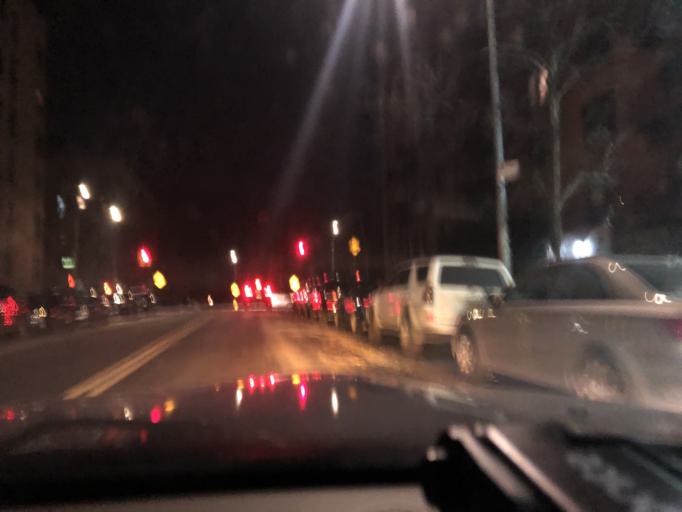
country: US
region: New York
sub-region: New York County
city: Inwood
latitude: 40.8687
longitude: -73.9218
